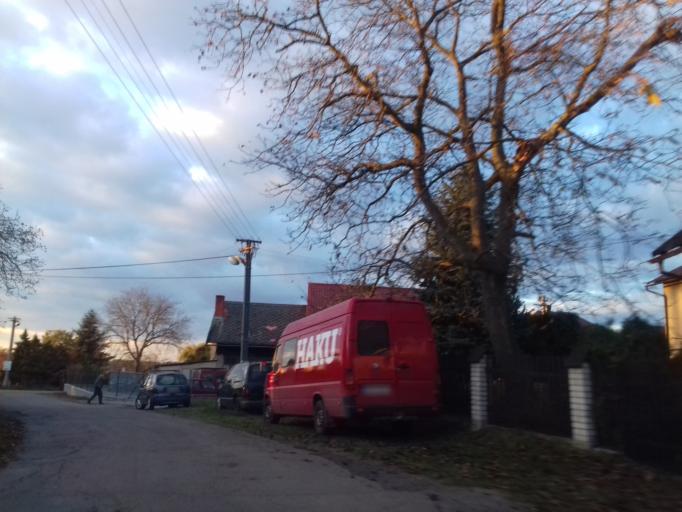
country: CZ
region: Pardubicky
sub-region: Okres Chrudim
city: Skutec
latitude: 49.8253
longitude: 15.9694
